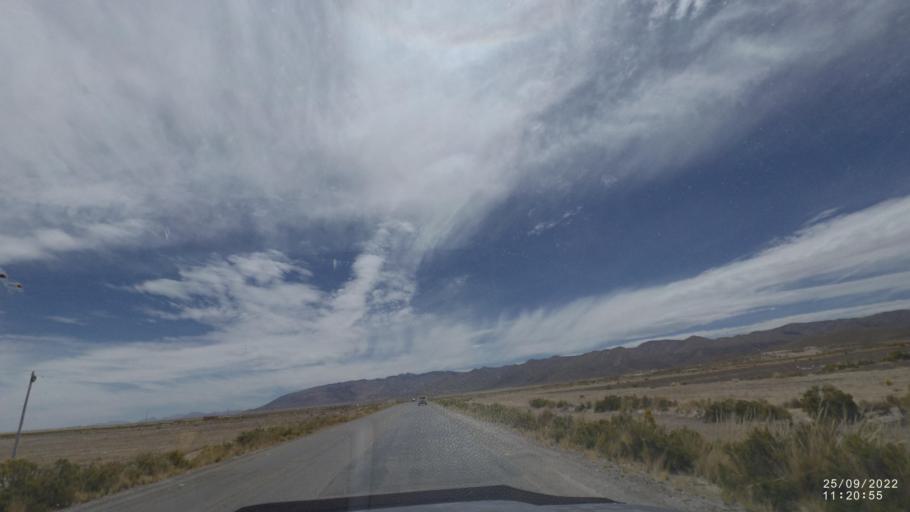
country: BO
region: Oruro
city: Challapata
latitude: -19.1511
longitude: -66.7729
